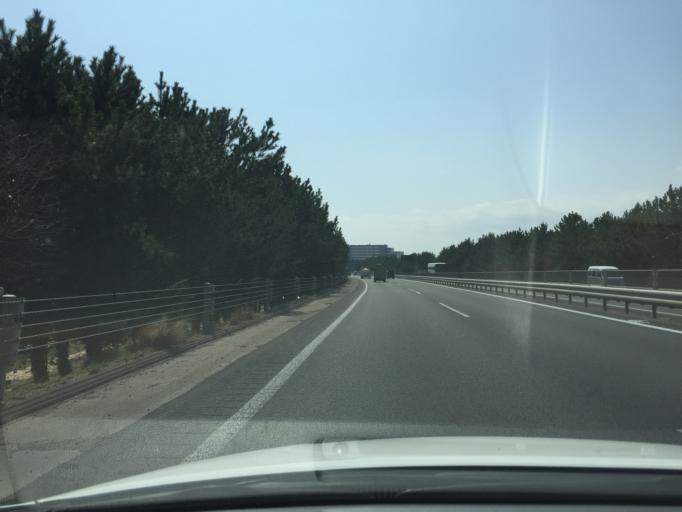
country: JP
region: Miyagi
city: Sendai-shi
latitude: 38.2430
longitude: 140.9524
